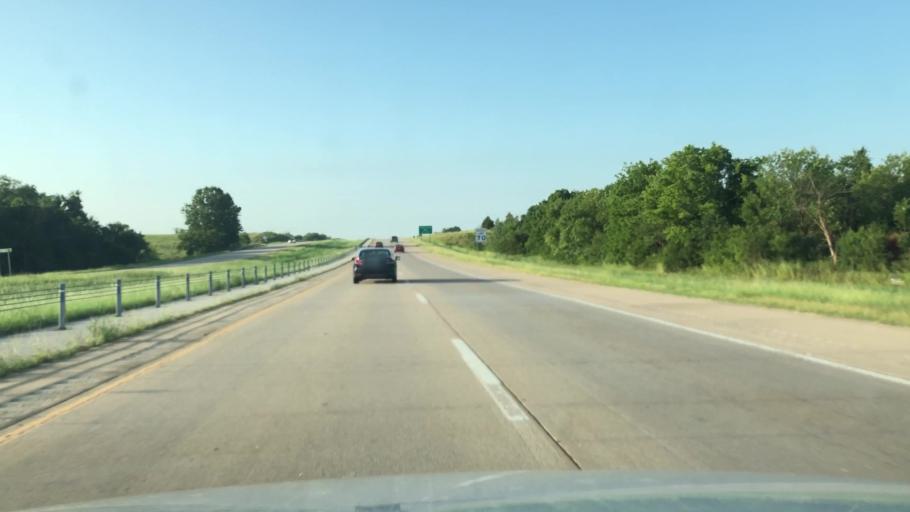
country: US
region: Oklahoma
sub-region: Washington County
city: Bartlesville
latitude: 36.5969
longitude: -95.9338
